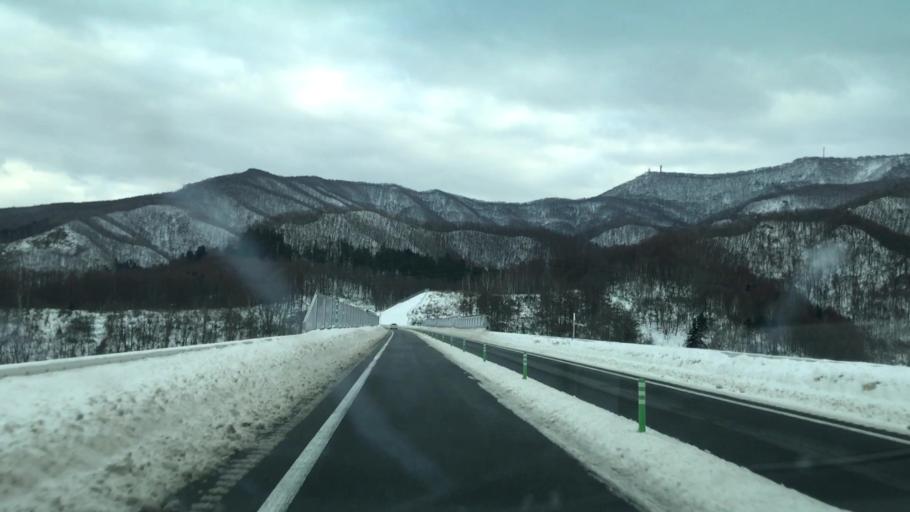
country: JP
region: Hokkaido
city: Otaru
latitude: 43.1657
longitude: 140.9868
